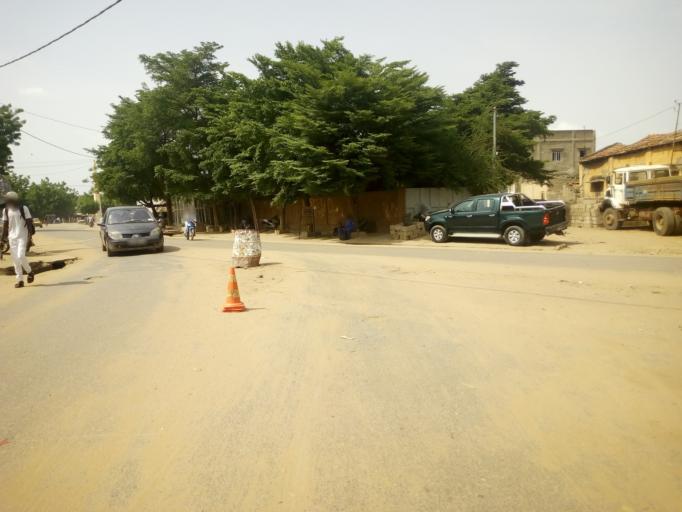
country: ML
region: Kayes
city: Kayes
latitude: 14.4450
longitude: -11.4385
